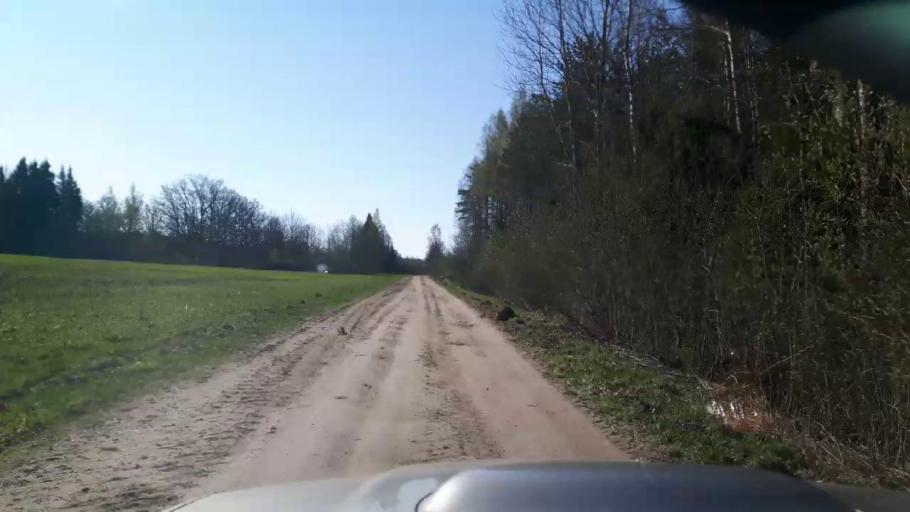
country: EE
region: Paernumaa
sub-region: Tootsi vald
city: Tootsi
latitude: 58.5055
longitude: 24.9385
